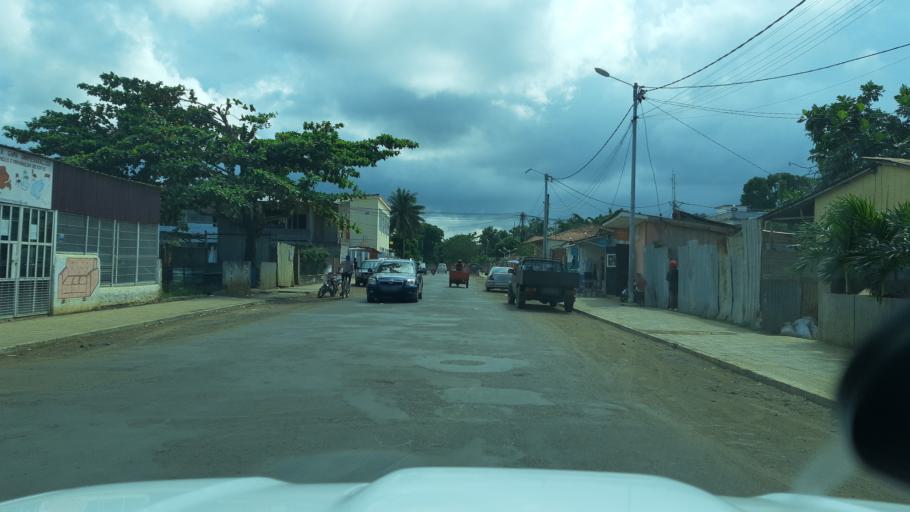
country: ST
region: Sao Tome Island
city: Sao Tome
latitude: 0.3368
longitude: 6.7354
